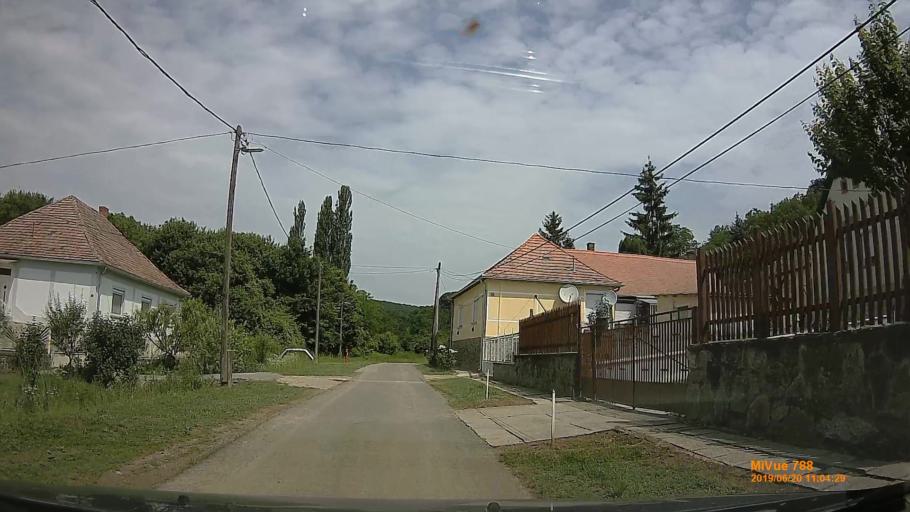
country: HU
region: Baranya
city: Mecseknadasd
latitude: 46.1842
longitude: 18.5116
